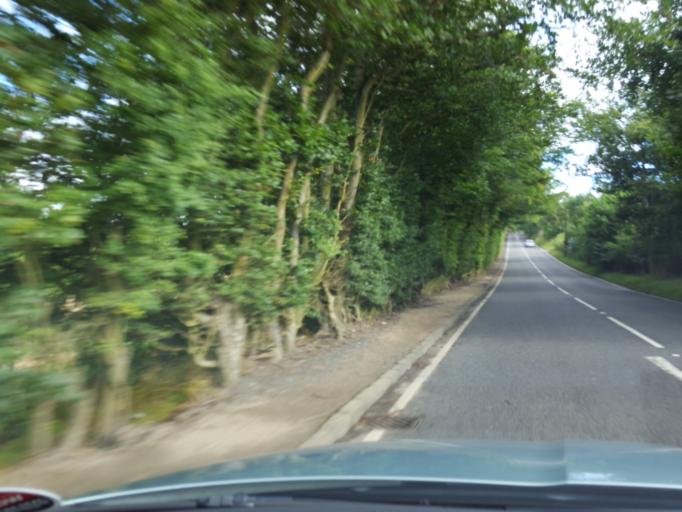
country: GB
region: Scotland
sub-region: West Lothian
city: Linlithgow
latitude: 55.9866
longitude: -3.6139
